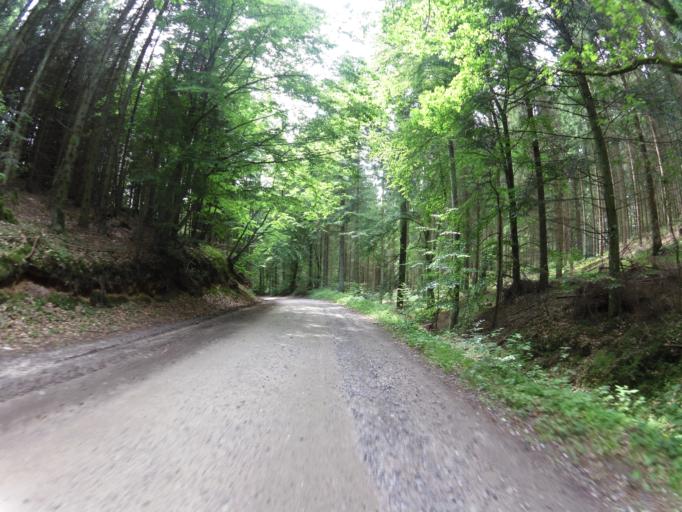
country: DK
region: North Denmark
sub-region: Bronderslev Kommune
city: Dronninglund
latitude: 57.1925
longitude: 10.2745
